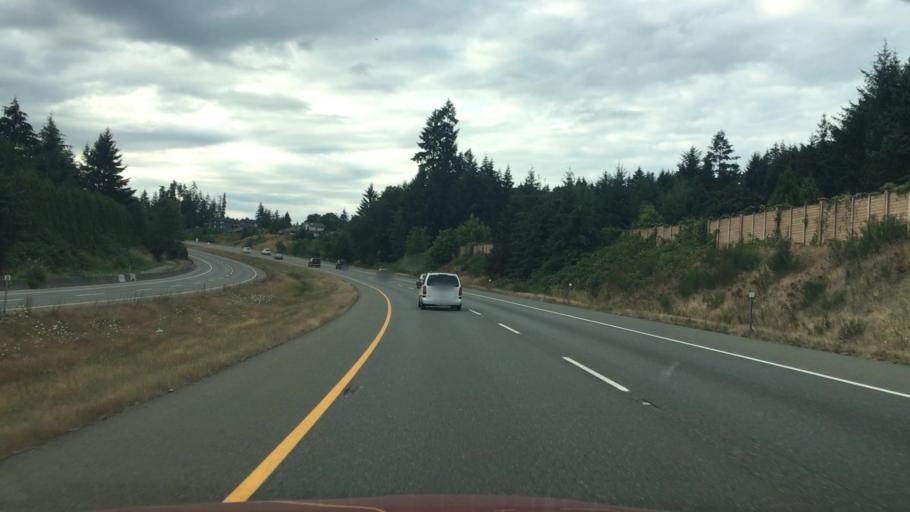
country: CA
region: British Columbia
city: Nanaimo
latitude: 49.2193
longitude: -124.0445
